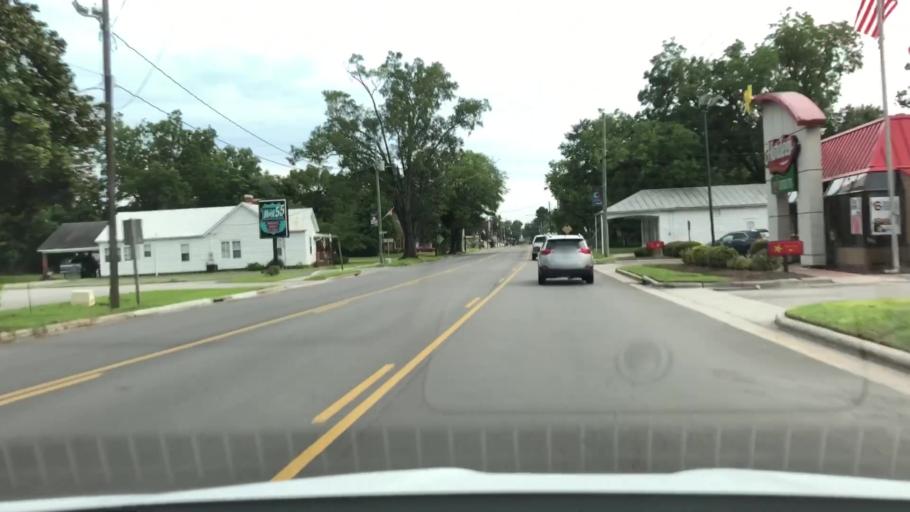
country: US
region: North Carolina
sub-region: Jones County
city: Maysville
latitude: 34.9020
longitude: -77.2315
